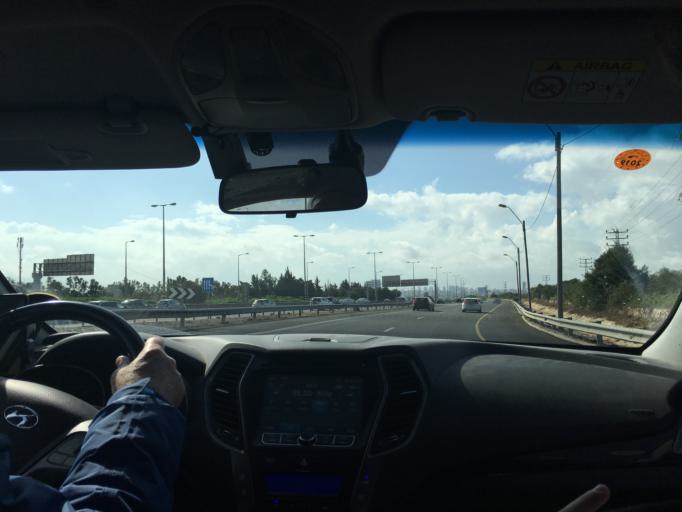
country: IL
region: Tel Aviv
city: Ramat HaSharon
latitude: 32.1235
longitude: 34.8540
